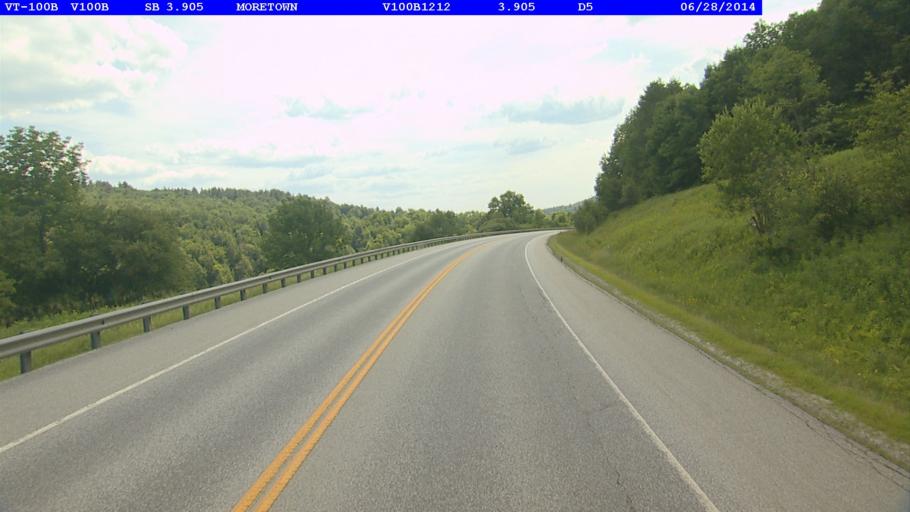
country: US
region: Vermont
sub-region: Washington County
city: Waterbury
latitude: 44.2825
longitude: -72.7352
